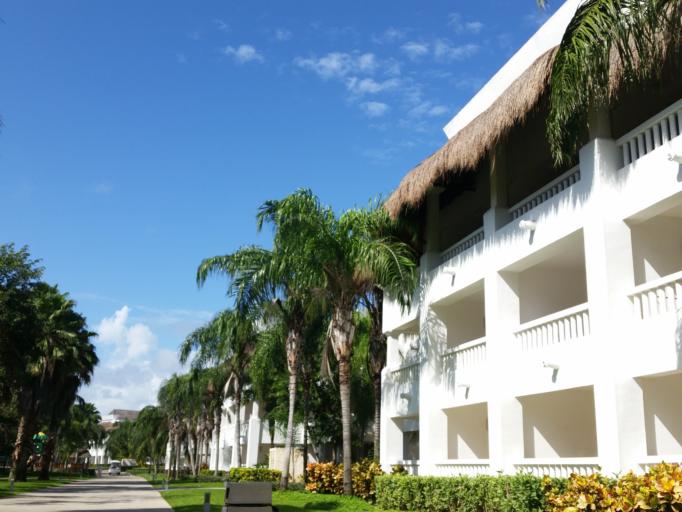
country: MX
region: Quintana Roo
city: Playa del Carmen
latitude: 20.6691
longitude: -87.0314
